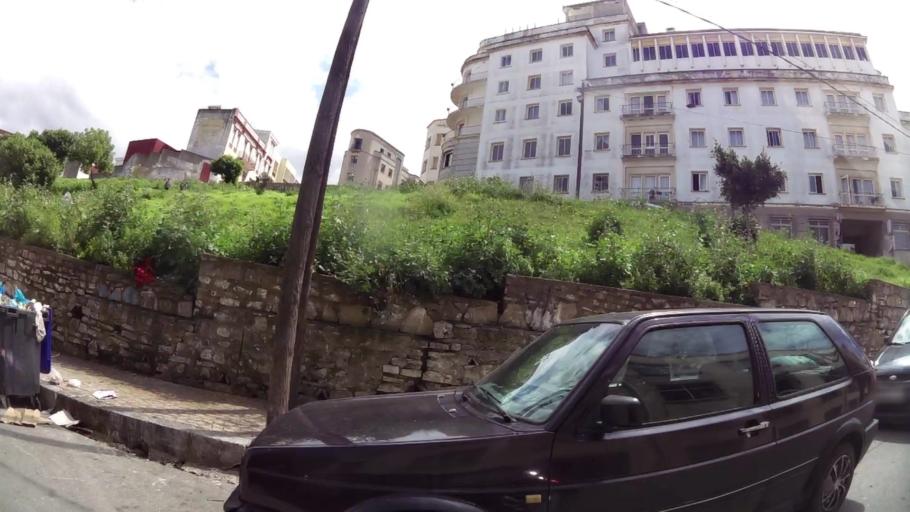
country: MA
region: Tanger-Tetouan
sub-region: Tanger-Assilah
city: Tangier
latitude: 35.7816
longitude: -5.8102
